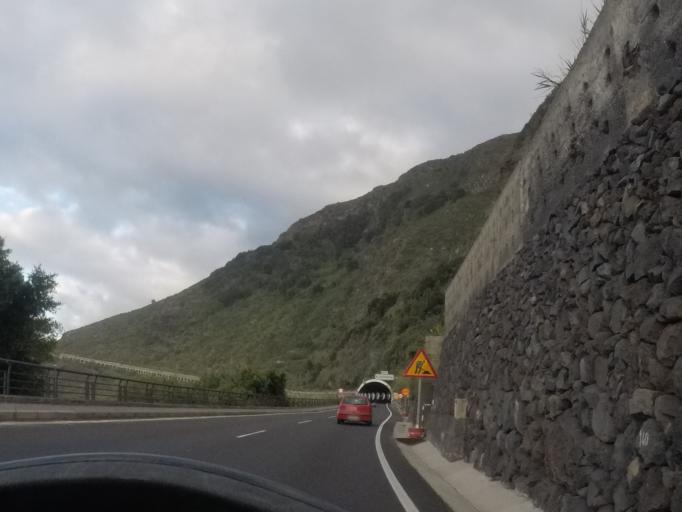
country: ES
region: Canary Islands
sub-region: Provincia de Santa Cruz de Tenerife
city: Garachico
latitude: 28.3708
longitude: -16.7544
